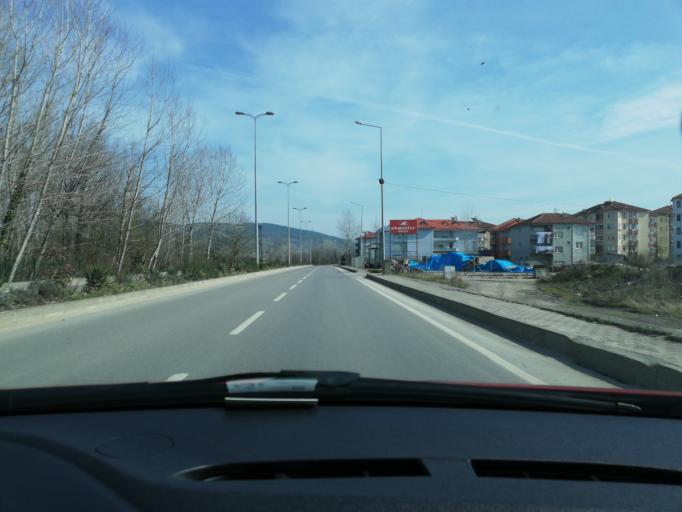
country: TR
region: Bartin
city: Bartin
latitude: 41.6372
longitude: 32.3507
